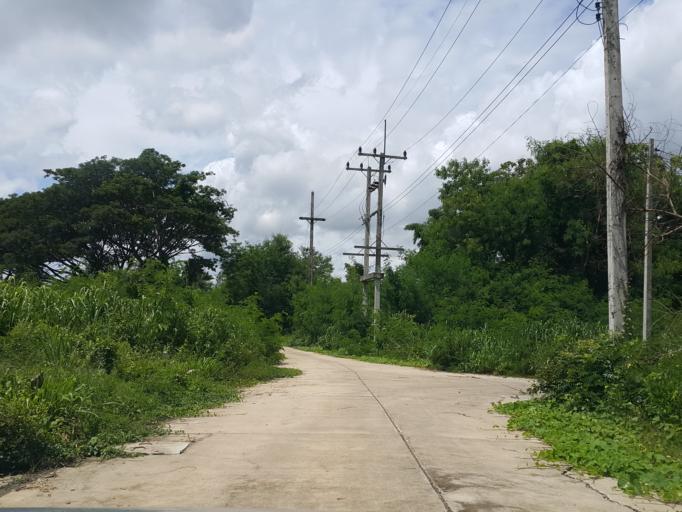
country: TH
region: Chiang Mai
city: San Kamphaeng
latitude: 18.7673
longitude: 99.1065
